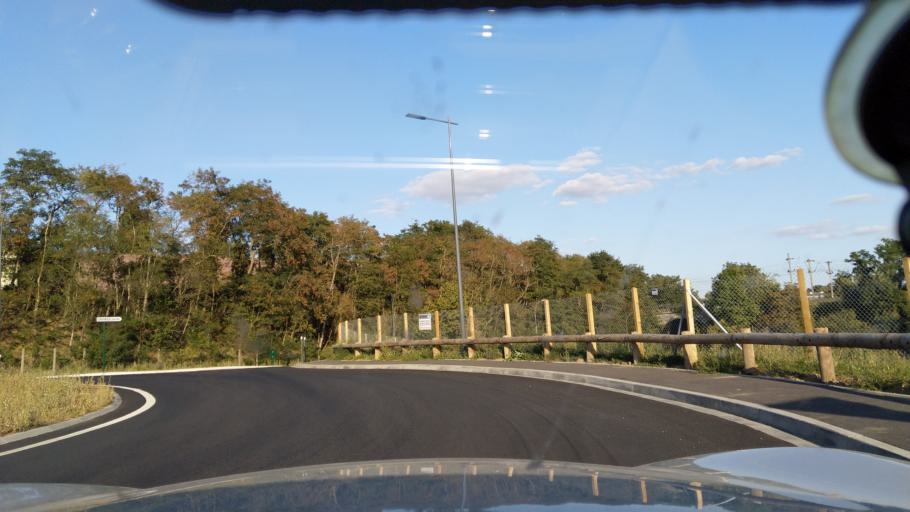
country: FR
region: Ile-de-France
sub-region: Departement du Val-d'Oise
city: Louvres
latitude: 49.0456
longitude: 2.4941
